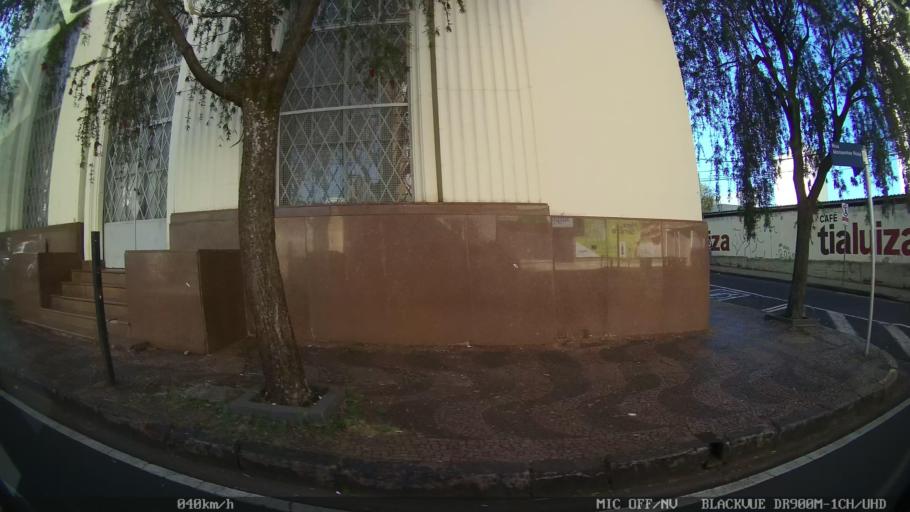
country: BR
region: Sao Paulo
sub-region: Franca
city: Franca
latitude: -20.5364
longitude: -47.4009
